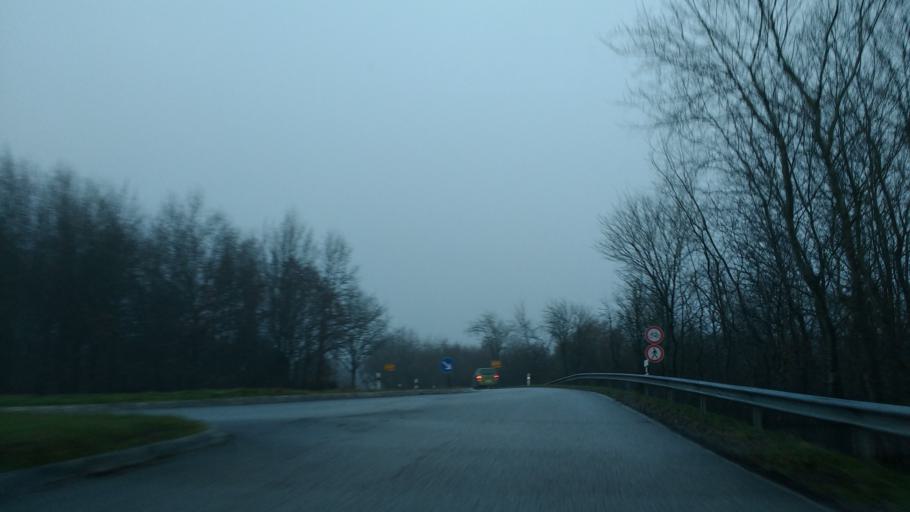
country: DE
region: Schleswig-Holstein
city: Osterronfeld
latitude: 54.2856
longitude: 9.6850
